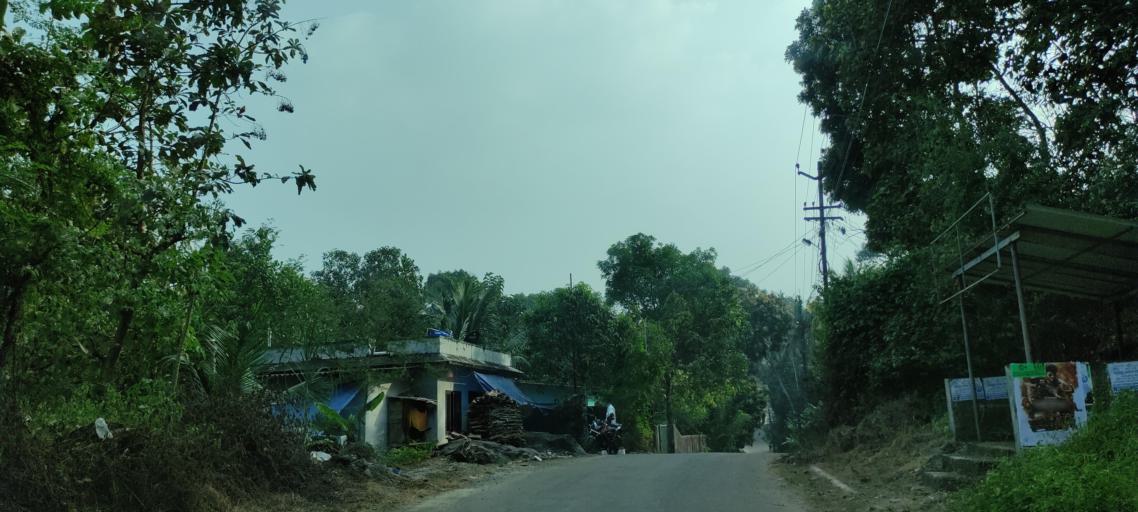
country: IN
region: Kerala
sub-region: Ernakulam
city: Piravam
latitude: 9.8008
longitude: 76.5356
